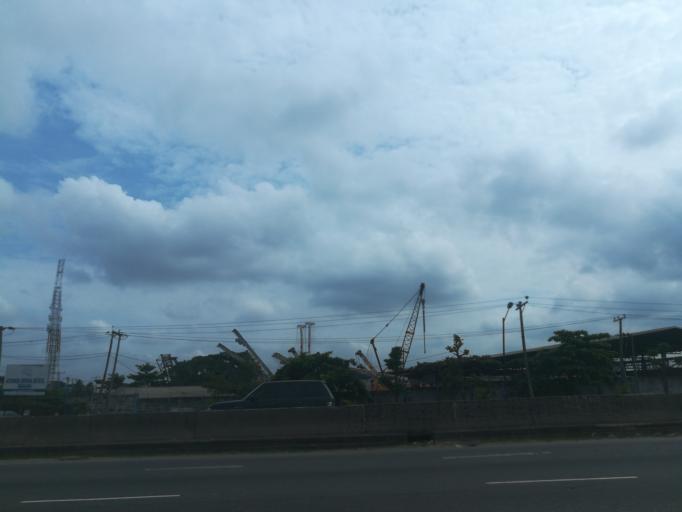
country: NG
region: Lagos
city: Somolu
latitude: 6.5481
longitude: 3.3803
